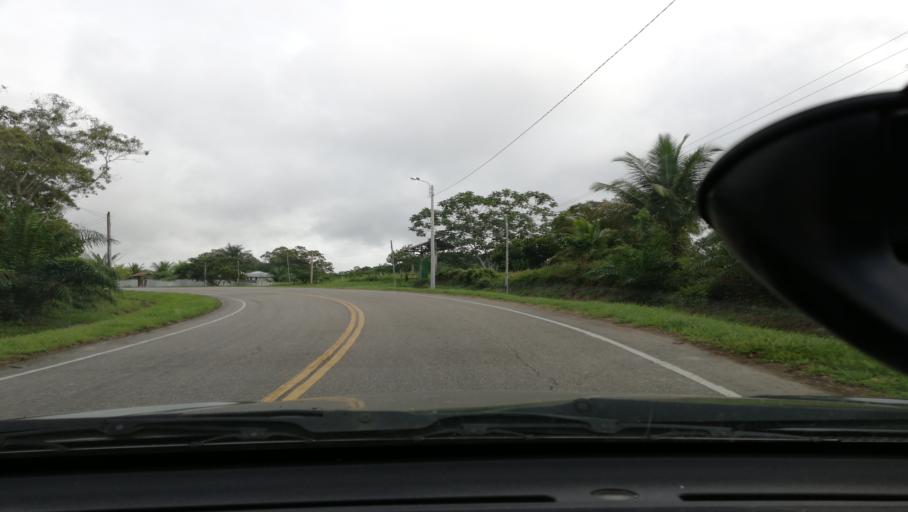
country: PE
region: Loreto
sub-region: Provincia de Loreto
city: Nauta
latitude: -4.4984
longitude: -73.5912
